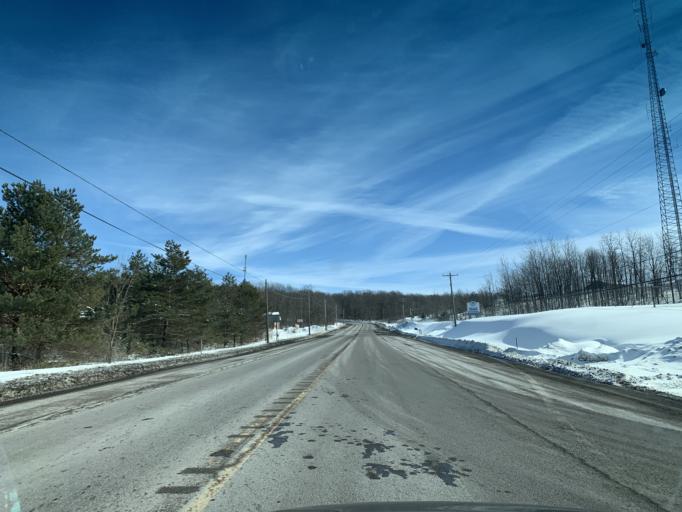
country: US
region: Pennsylvania
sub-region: Somerset County
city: Meyersdale
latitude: 39.6900
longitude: -79.0926
